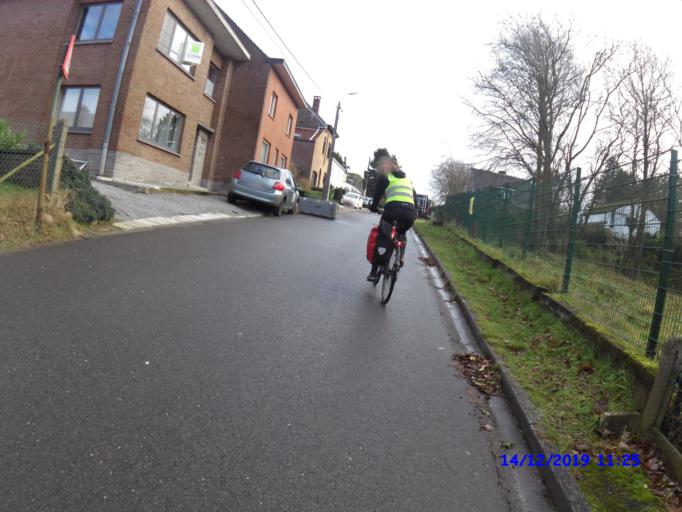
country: BE
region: Flanders
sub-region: Provincie Vlaams-Brabant
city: Beersel
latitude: 50.7284
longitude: 4.3145
